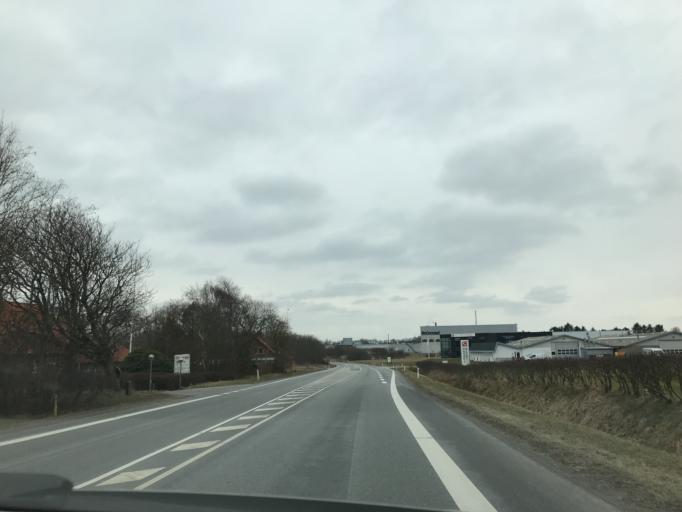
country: DK
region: South Denmark
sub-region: Varde Kommune
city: Olgod
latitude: 55.8112
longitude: 8.6401
